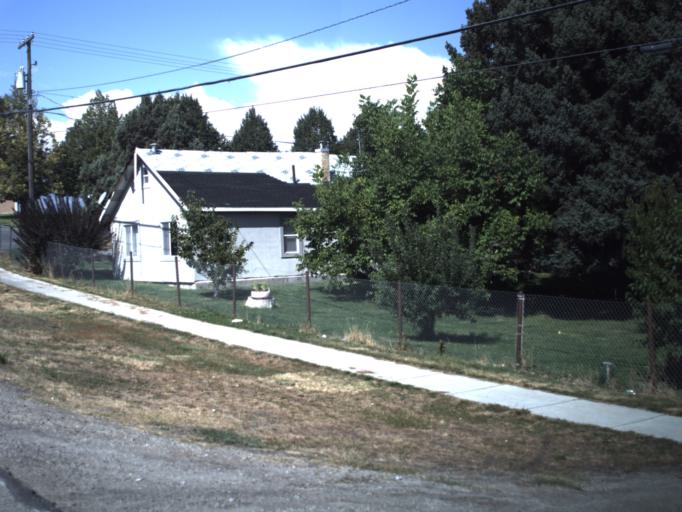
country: US
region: Utah
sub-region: Cache County
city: Hyrum
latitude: 41.6343
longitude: -111.8657
